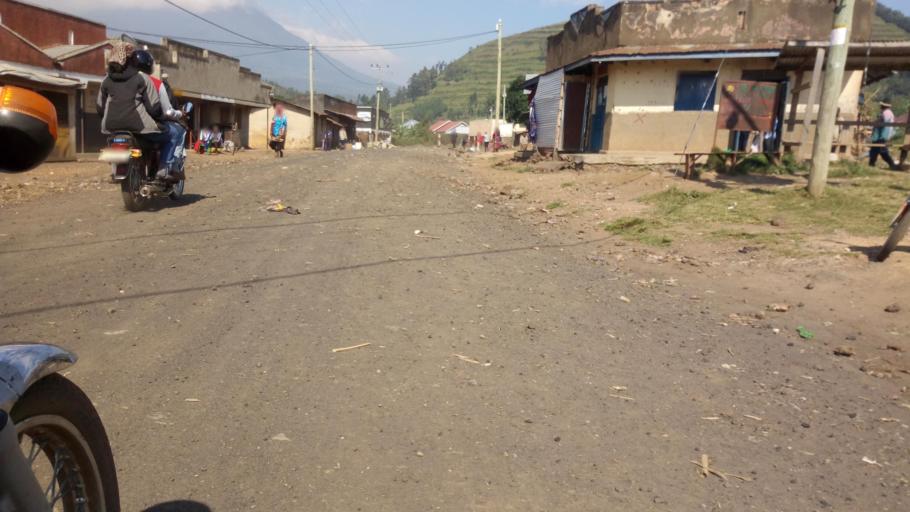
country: UG
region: Western Region
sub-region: Kisoro District
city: Kisoro
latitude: -1.3323
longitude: 29.6387
